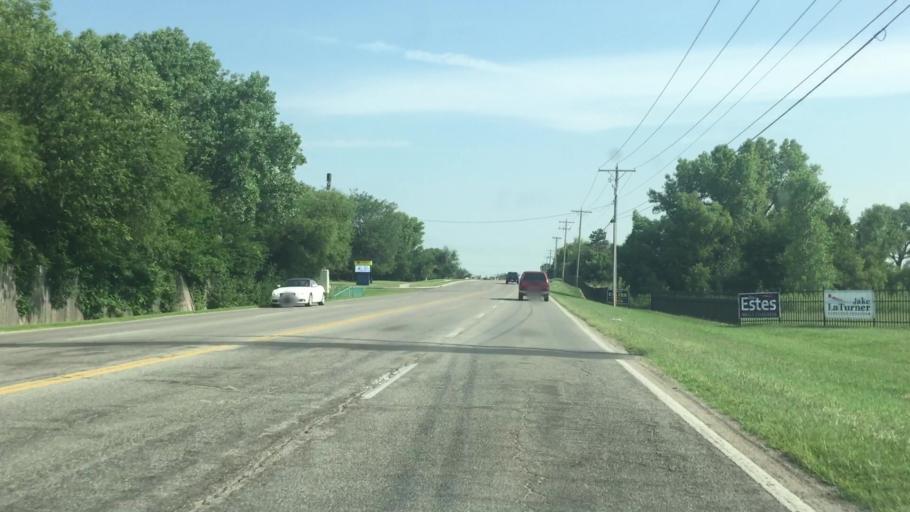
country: US
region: Kansas
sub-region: Sedgwick County
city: Bellaire
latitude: 37.7048
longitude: -97.2262
